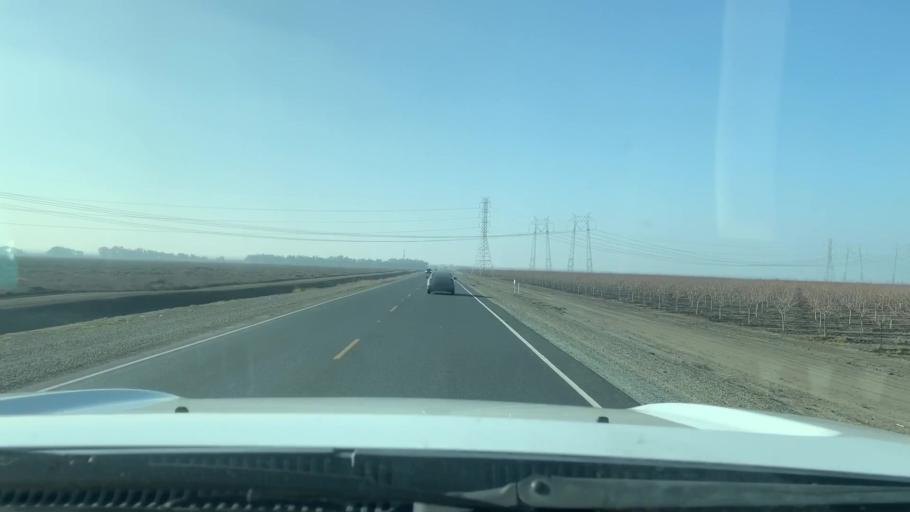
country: US
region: California
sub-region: Kern County
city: Lost Hills
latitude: 35.6161
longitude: -119.6223
